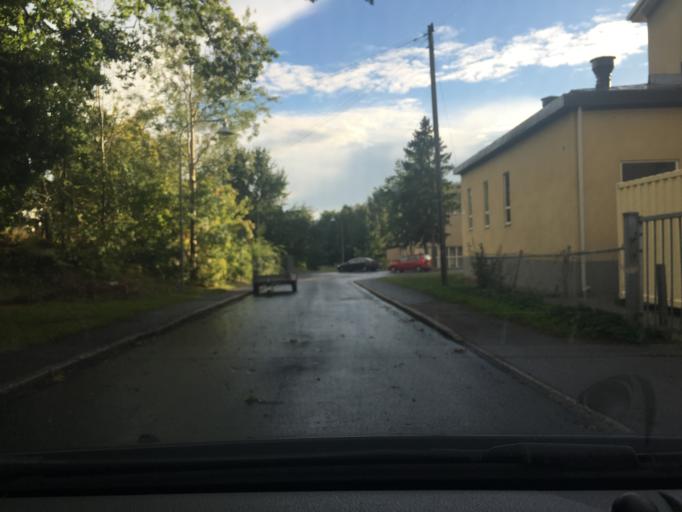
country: SE
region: Stockholm
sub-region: Stockholms Kommun
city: Bromma
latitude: 59.3319
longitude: 17.9630
